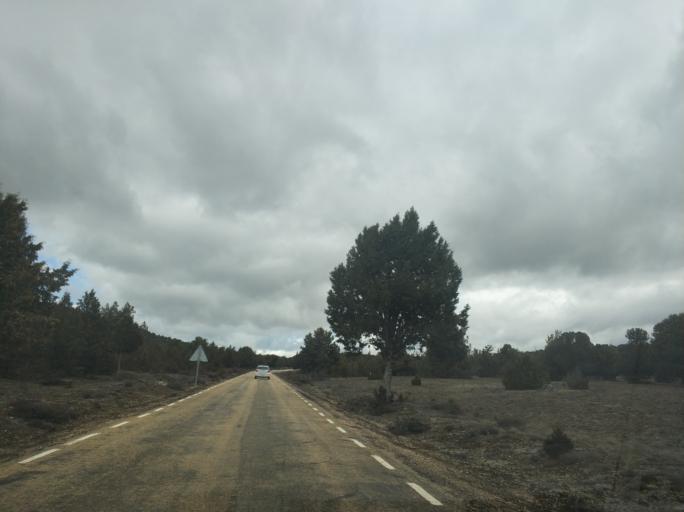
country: ES
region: Castille and Leon
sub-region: Provincia de Soria
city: Abejar
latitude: 41.7777
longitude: -2.7766
